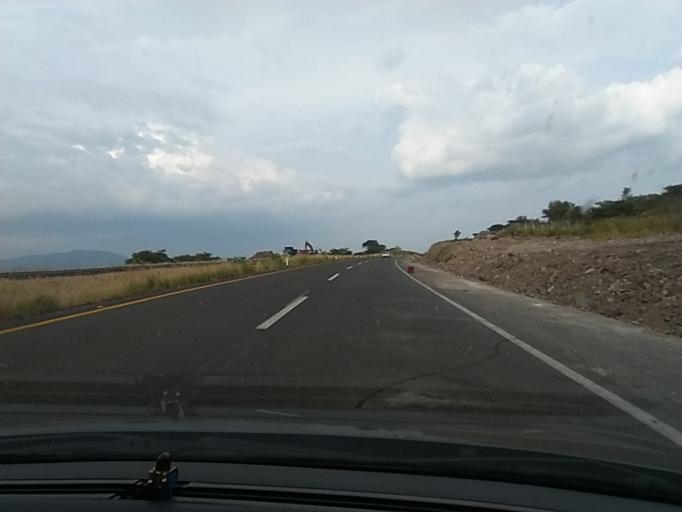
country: MX
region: Mexico
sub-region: Chapultepec
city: Chucandiro
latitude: 19.9031
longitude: -101.2944
